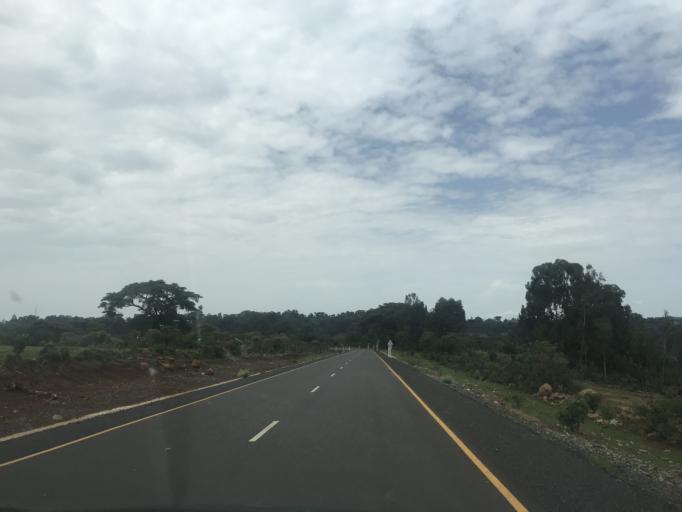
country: ET
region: Oromiya
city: Shambu
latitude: 9.8739
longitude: 36.6753
